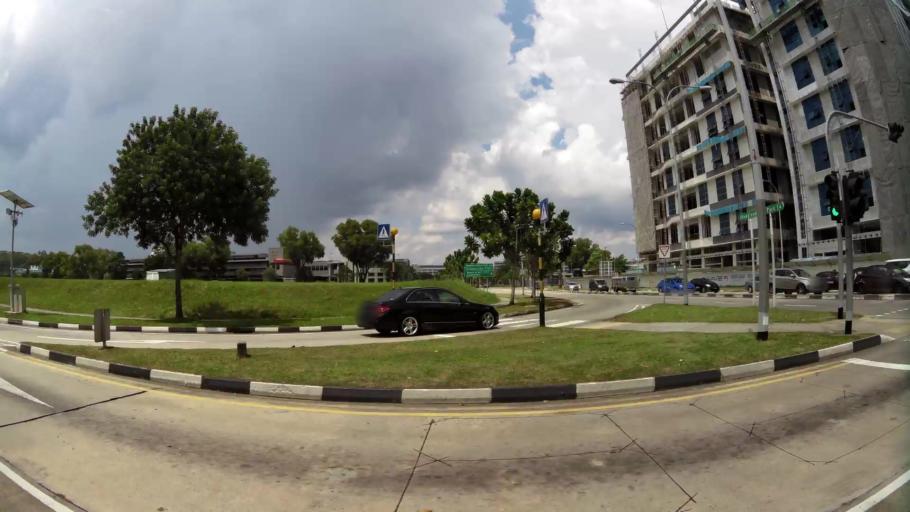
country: MY
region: Johor
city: Johor Bahru
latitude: 1.4475
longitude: 103.7967
